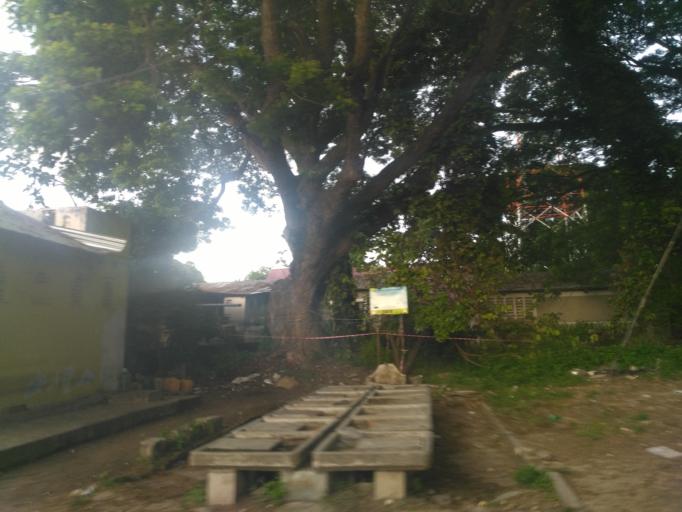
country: TZ
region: Zanzibar Urban/West
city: Zanzibar
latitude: -6.1660
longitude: 39.1937
